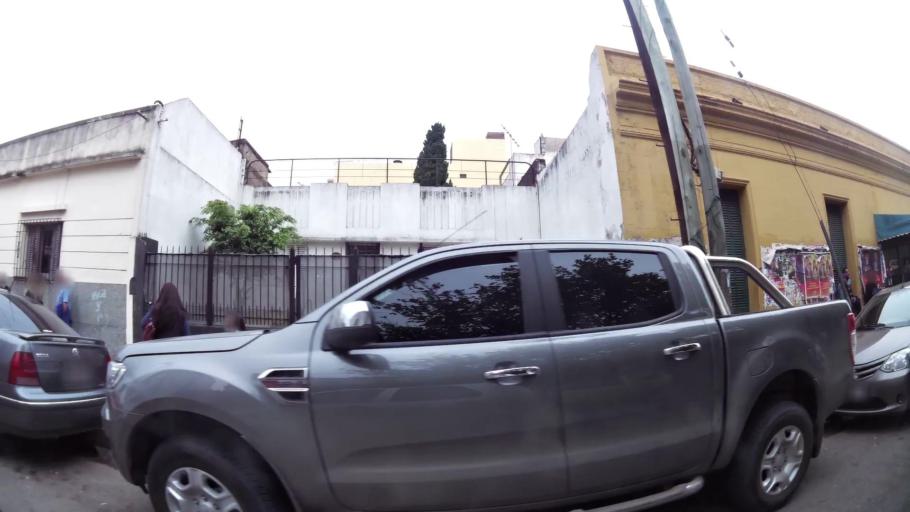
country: AR
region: Buenos Aires
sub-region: Partido de Lanus
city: Lanus
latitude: -34.7116
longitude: -58.3845
